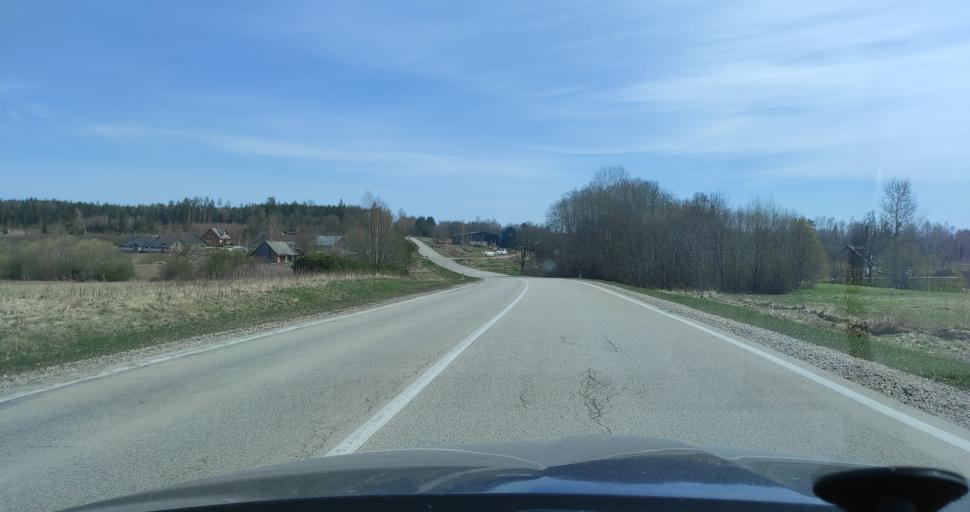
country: LV
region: Talsu Rajons
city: Stende
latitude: 57.1910
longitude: 22.3785
